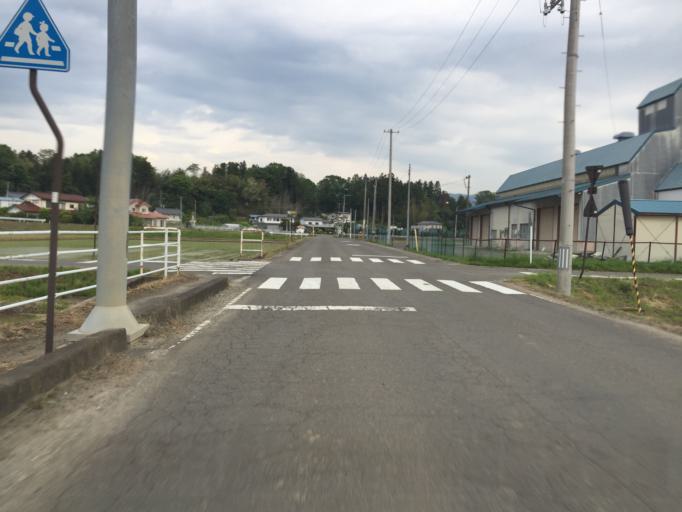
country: JP
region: Fukushima
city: Hobaramachi
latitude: 37.8474
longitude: 140.5370
